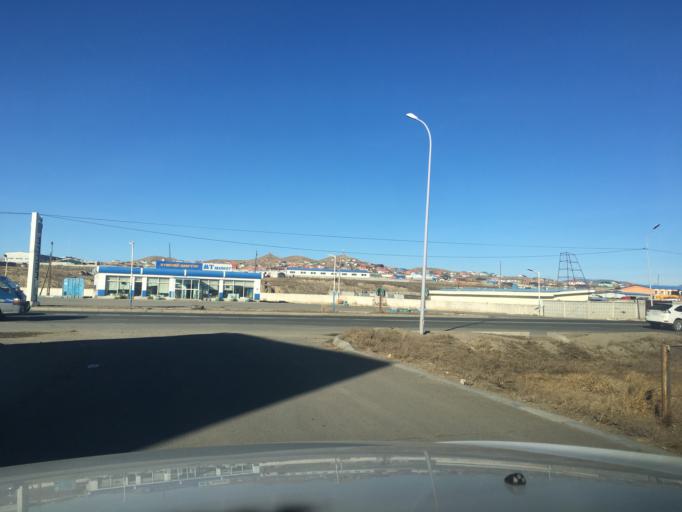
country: MN
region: Ulaanbaatar
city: Ulaanbaatar
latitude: 47.9006
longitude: 106.7219
